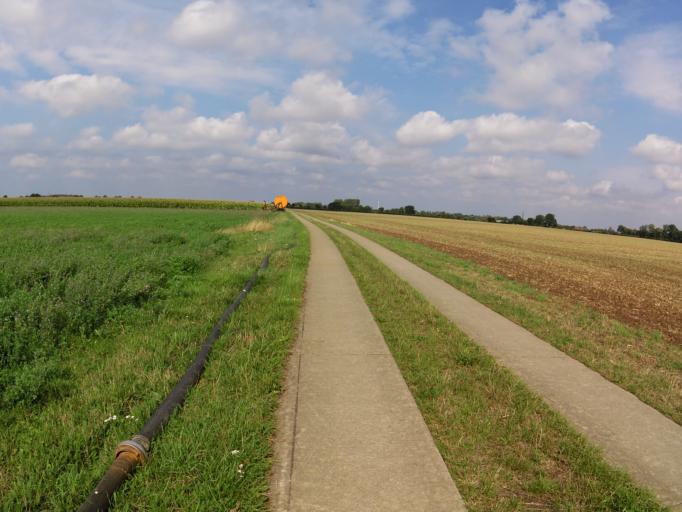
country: DE
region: Lower Saxony
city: Bucken
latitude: 52.7859
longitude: 9.1435
